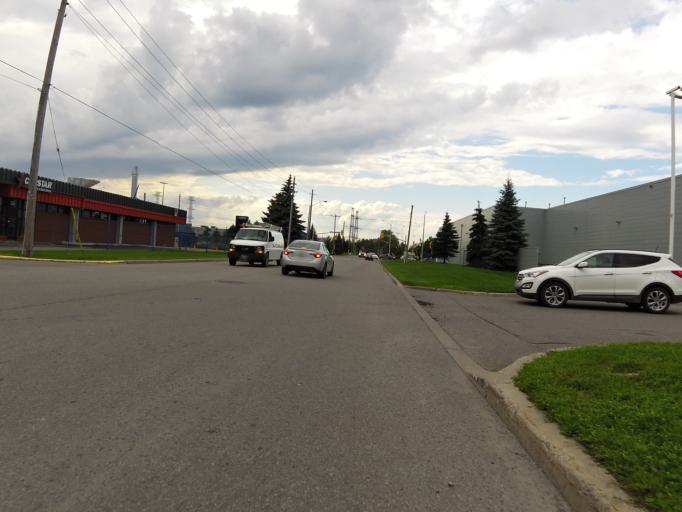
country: CA
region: Ontario
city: Ottawa
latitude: 45.3357
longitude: -75.7185
